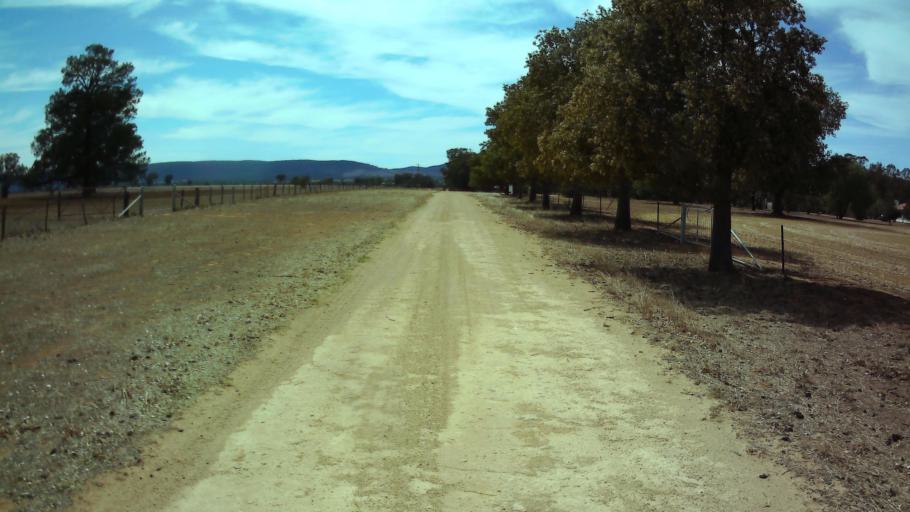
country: AU
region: New South Wales
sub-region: Weddin
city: Grenfell
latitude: -33.7207
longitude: 148.2628
